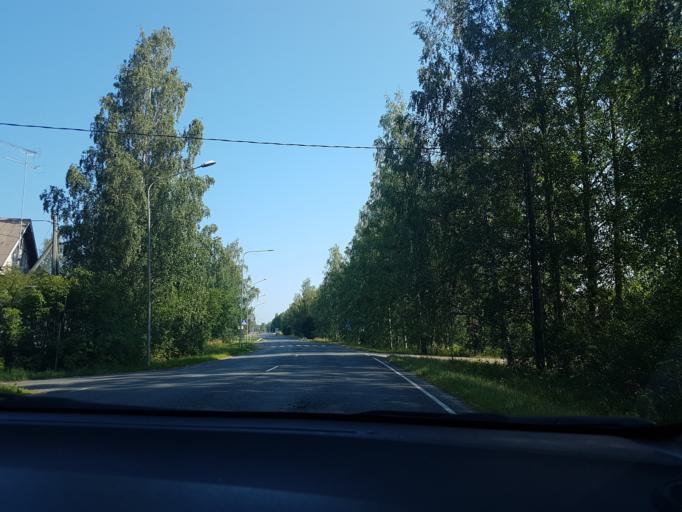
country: FI
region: Uusimaa
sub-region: Helsinki
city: Kerava
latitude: 60.3894
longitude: 25.1000
